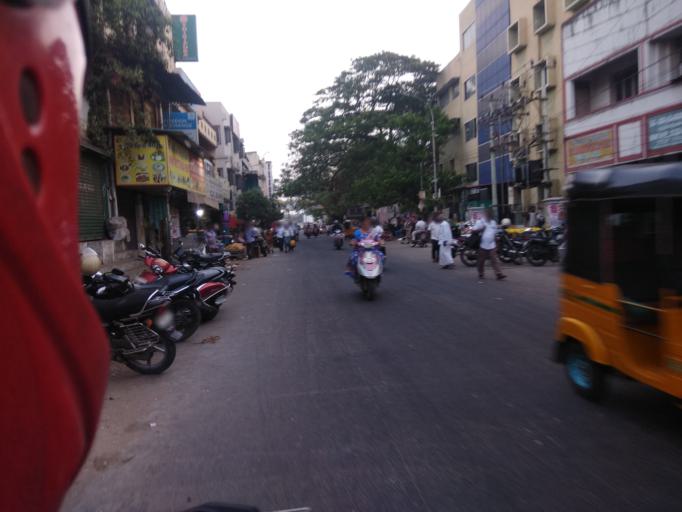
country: IN
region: Tamil Nadu
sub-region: Kancheepuram
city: Alandur
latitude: 13.0213
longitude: 80.2243
